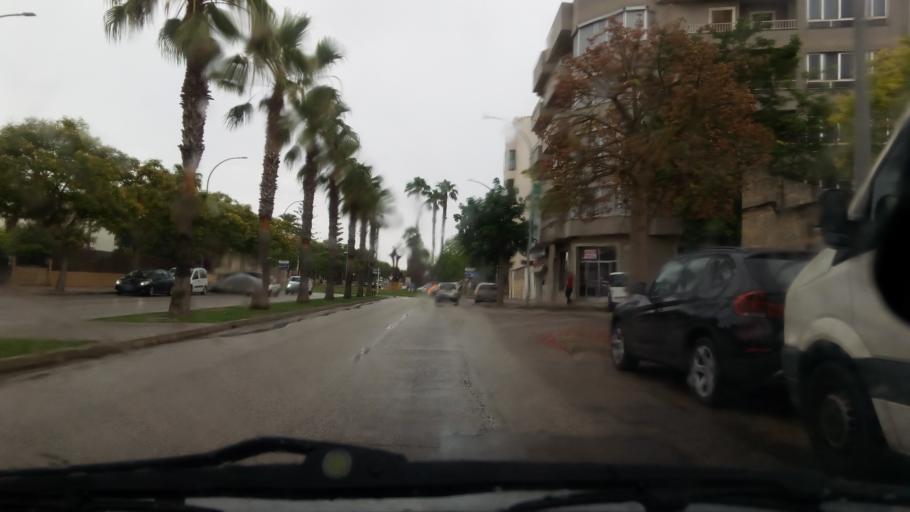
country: ES
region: Balearic Islands
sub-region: Illes Balears
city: Manacor
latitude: 39.5709
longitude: 3.2185
